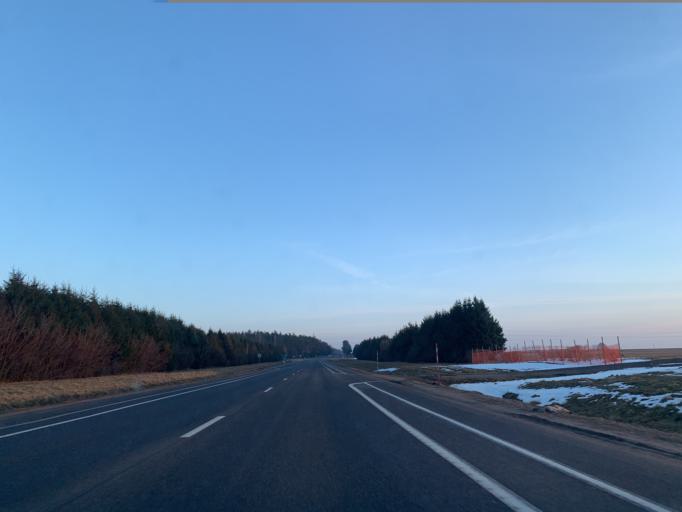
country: BY
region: Minsk
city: Haradzyeya
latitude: 53.2880
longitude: 26.5819
